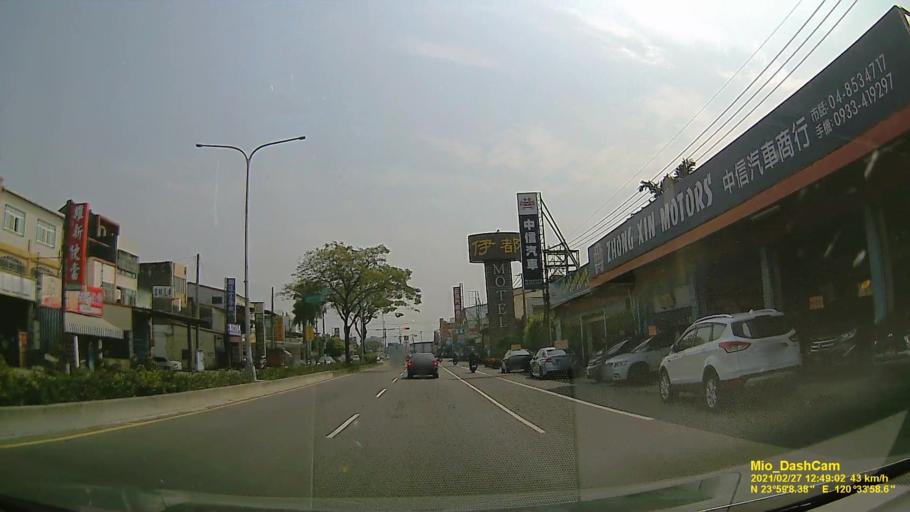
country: TW
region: Taiwan
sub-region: Changhua
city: Chang-hua
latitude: 23.9857
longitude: 120.5663
